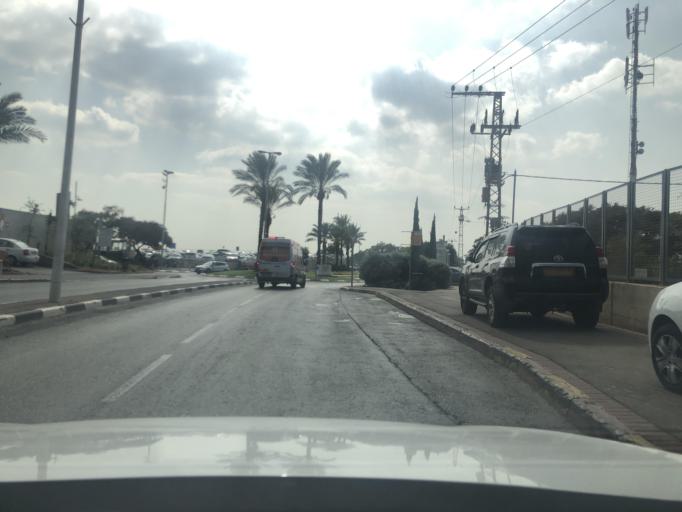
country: IL
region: Tel Aviv
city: Or Yehuda
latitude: 32.0460
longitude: 34.8410
